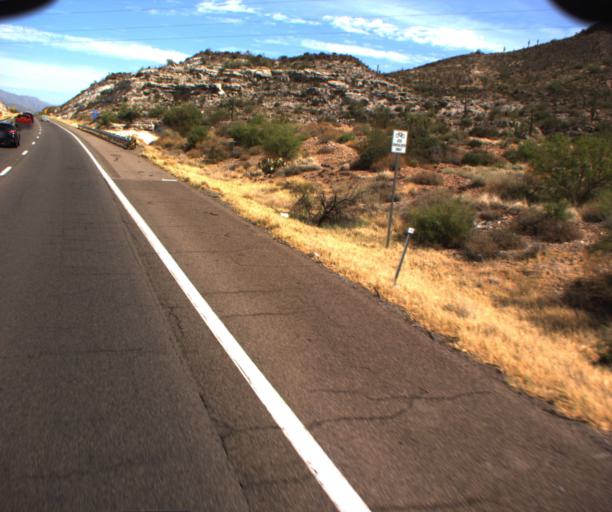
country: US
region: Arizona
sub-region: Maricopa County
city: New River
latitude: 33.9742
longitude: -112.1274
